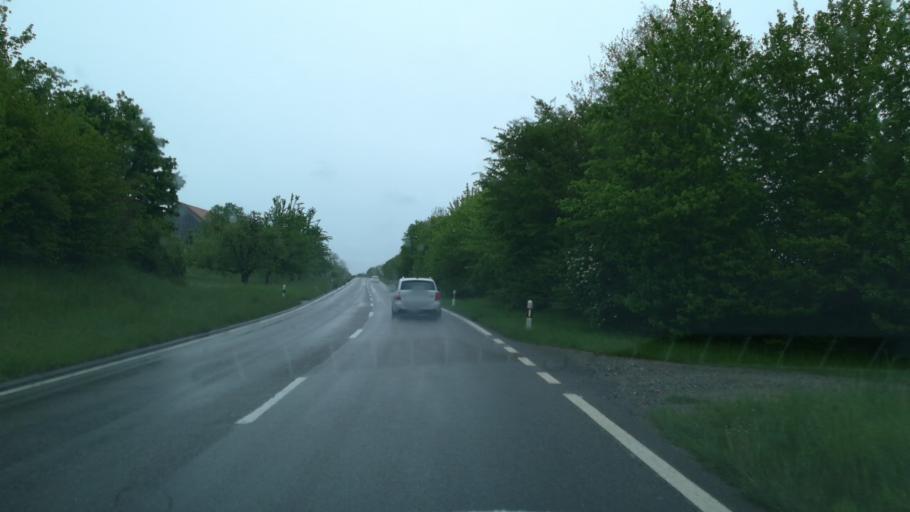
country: CH
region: Thurgau
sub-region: Weinfelden District
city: Wigoltingen
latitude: 47.6112
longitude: 9.0492
